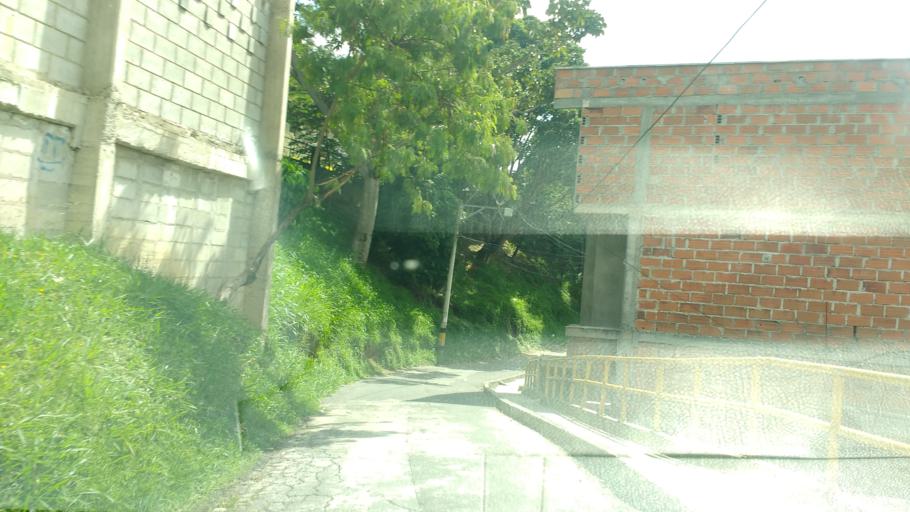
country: CO
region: Antioquia
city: Medellin
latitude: 6.2613
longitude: -75.6114
